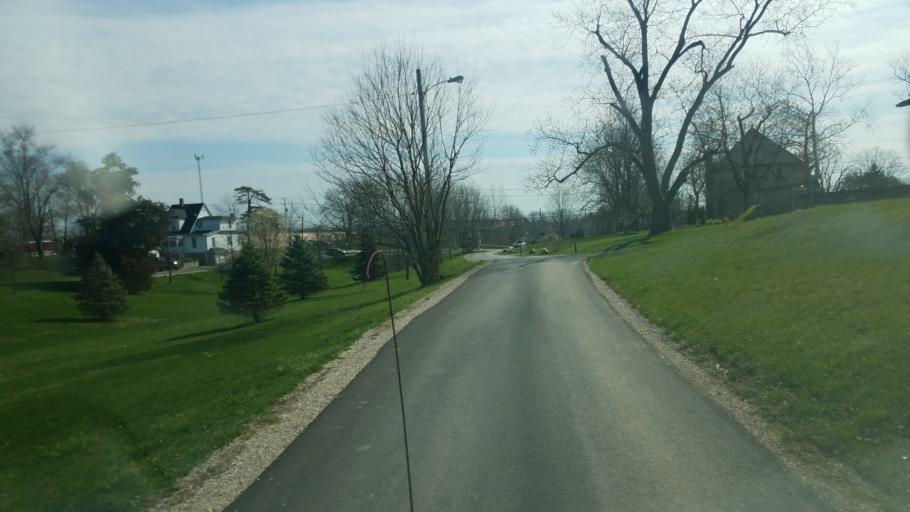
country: US
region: Ohio
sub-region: Delaware County
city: Delaware
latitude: 40.2845
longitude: -83.0706
